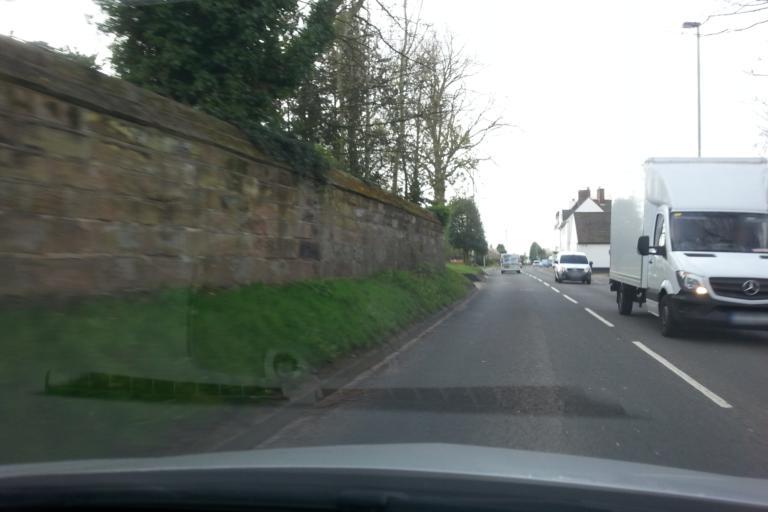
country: GB
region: England
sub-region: Staffordshire
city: Shenstone
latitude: 52.6406
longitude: -1.8348
